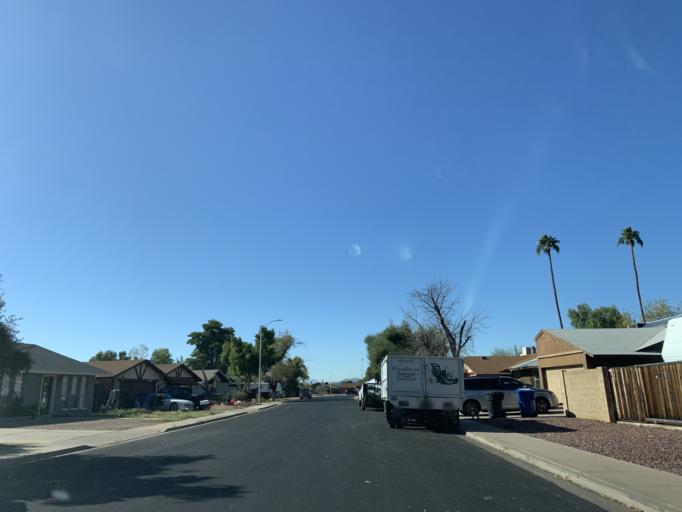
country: US
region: Arizona
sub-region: Maricopa County
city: San Carlos
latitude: 33.3621
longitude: -111.8610
